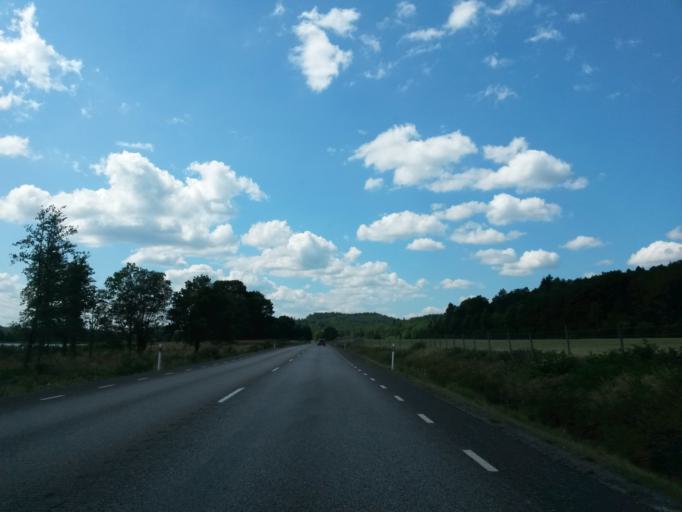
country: SE
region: Vaestra Goetaland
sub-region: Alingsas Kommun
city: Alingsas
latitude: 57.9666
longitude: 12.4130
